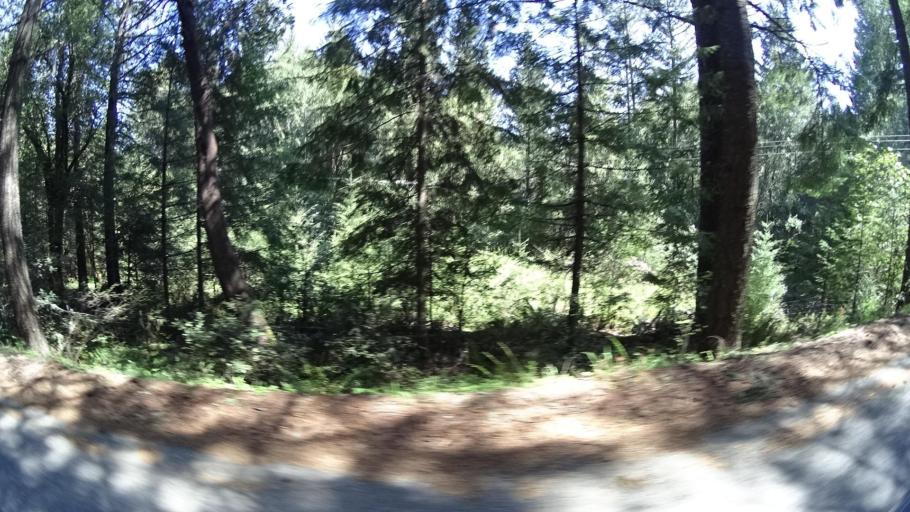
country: US
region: California
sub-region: Humboldt County
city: Redway
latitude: 40.0375
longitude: -123.6414
